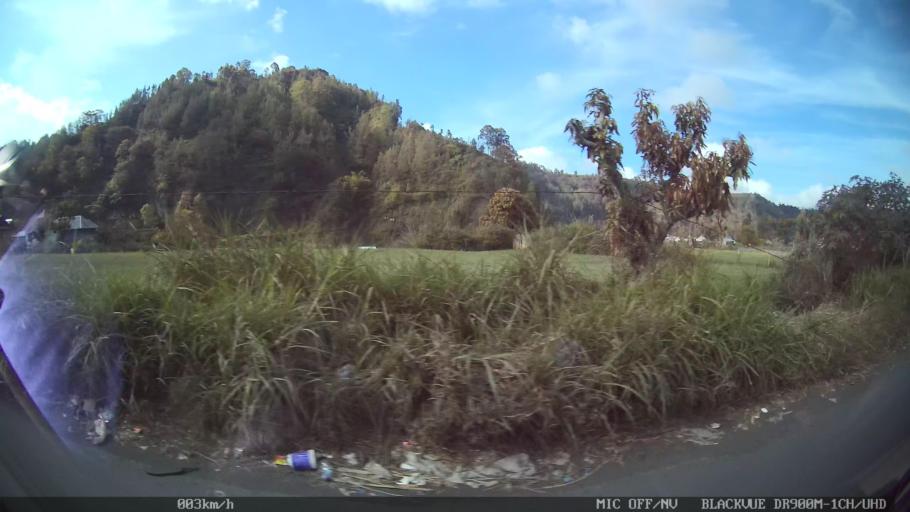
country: ID
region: Bali
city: Banjar Trunyan
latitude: -8.2155
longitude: 115.3758
